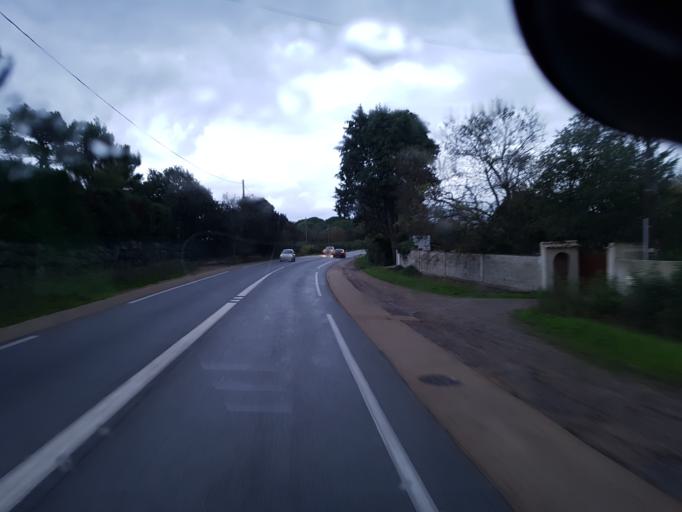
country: FR
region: Provence-Alpes-Cote d'Azur
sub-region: Departement du Var
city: Gassin
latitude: 43.2552
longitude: 6.5746
